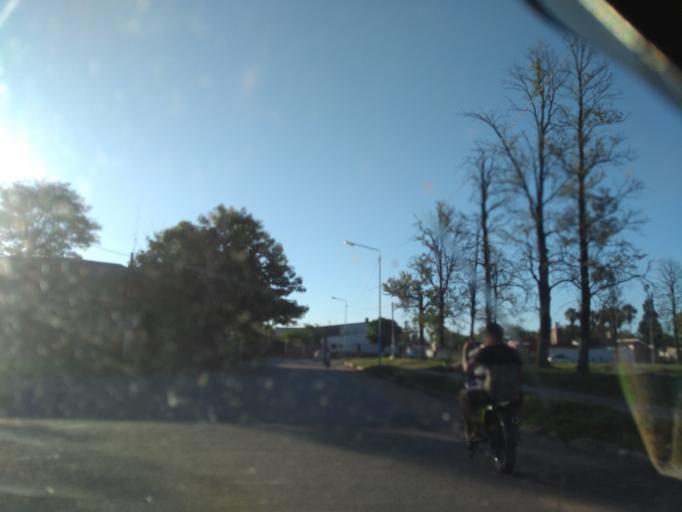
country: AR
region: Chaco
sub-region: Departamento de Quitilipi
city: Quitilipi
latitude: -26.8730
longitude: -60.2206
